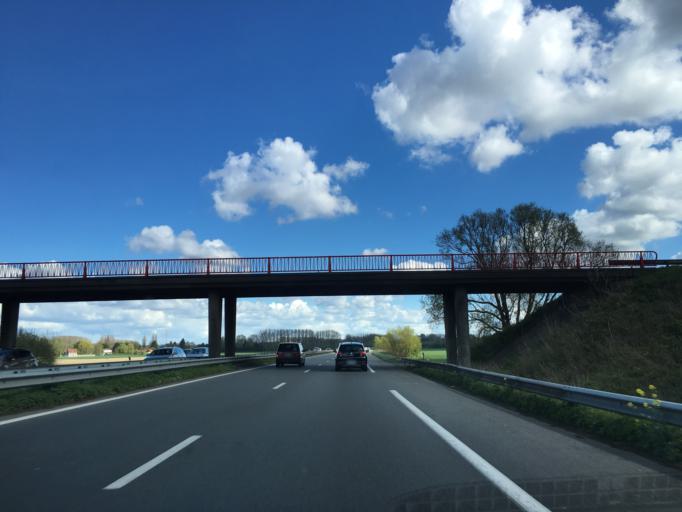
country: FR
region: Nord-Pas-de-Calais
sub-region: Departement du Nord
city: Ennetieres-en-Weppes
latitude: 50.6517
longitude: 2.9182
